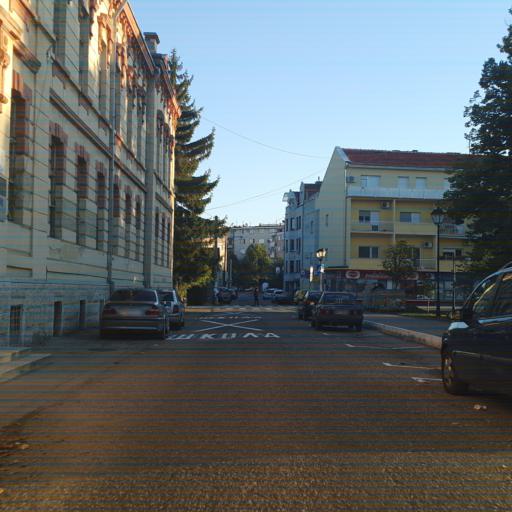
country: RS
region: Central Serbia
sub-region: Borski Okrug
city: Negotin
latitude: 44.2269
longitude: 22.5292
